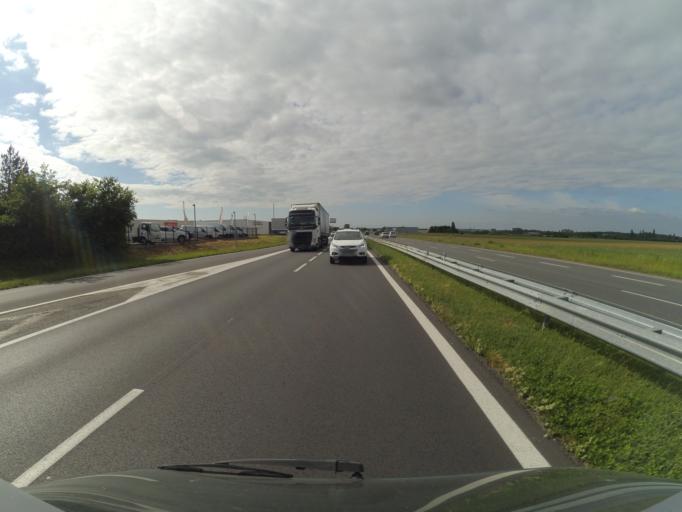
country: FR
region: Poitou-Charentes
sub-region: Departement de la Charente-Maritime
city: Angoulins
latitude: 46.1060
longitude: -1.0975
